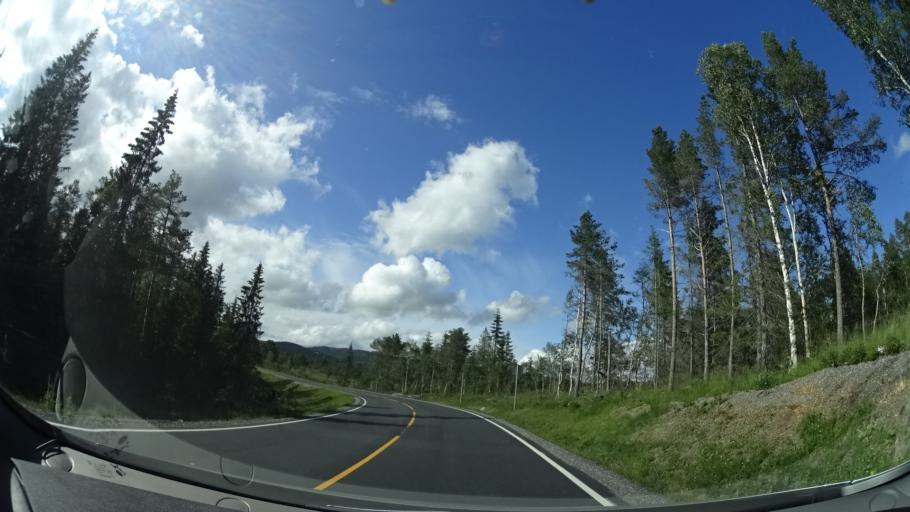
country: NO
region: Sor-Trondelag
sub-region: Snillfjord
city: Krokstadora
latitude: 63.2330
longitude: 9.5602
